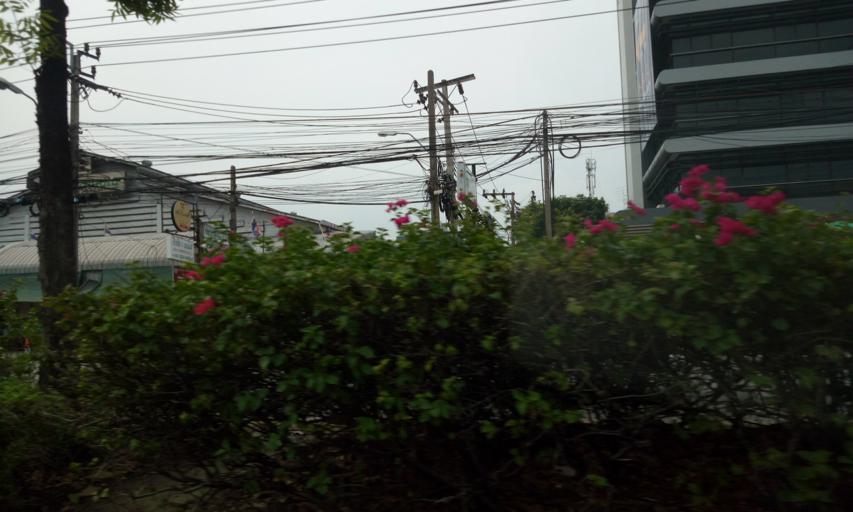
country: TH
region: Bangkok
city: Saphan Sung
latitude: 13.7222
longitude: 100.7193
